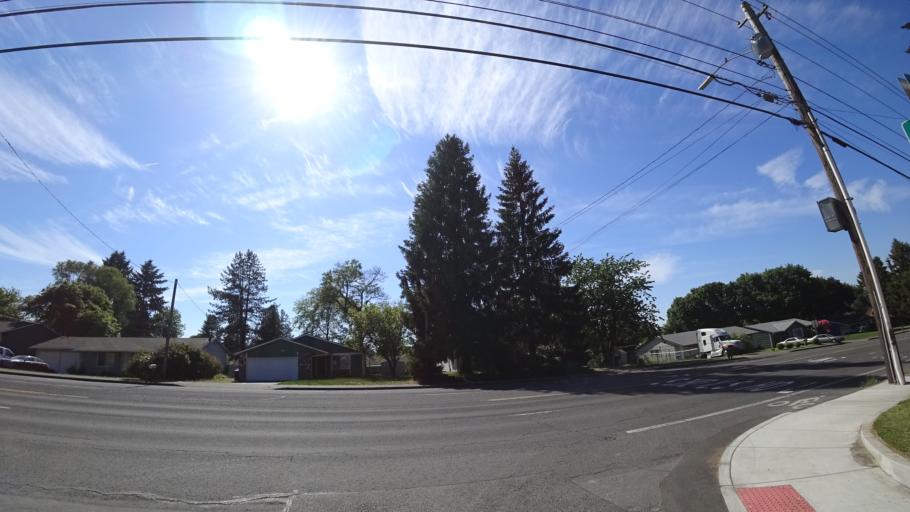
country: US
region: Oregon
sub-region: Multnomah County
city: Gresham
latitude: 45.4993
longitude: -122.4754
